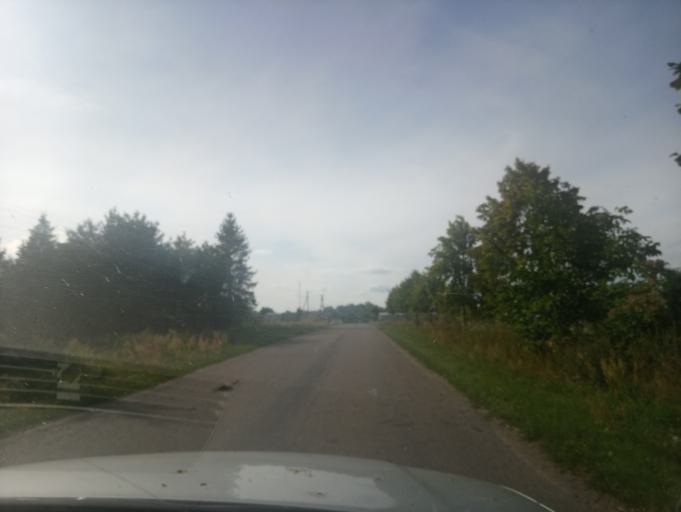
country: PL
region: Greater Poland Voivodeship
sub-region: Powiat pilski
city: Lobzenica
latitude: 53.2270
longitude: 17.3283
